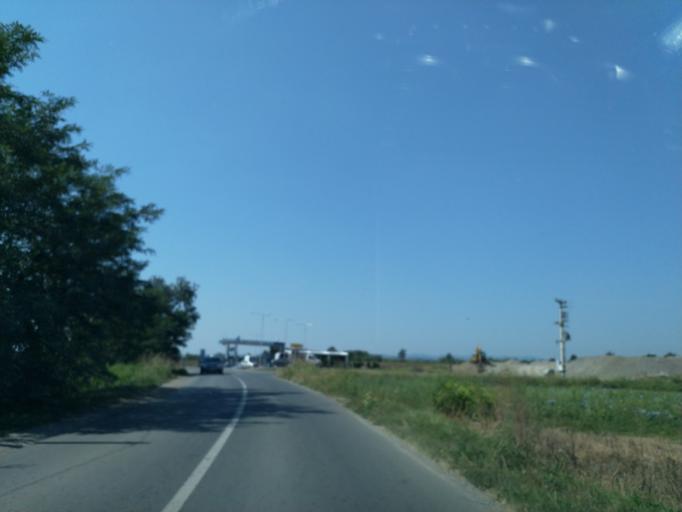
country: RS
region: Central Serbia
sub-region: Rasinski Okrug
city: Krusevac
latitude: 43.6194
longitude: 21.1816
